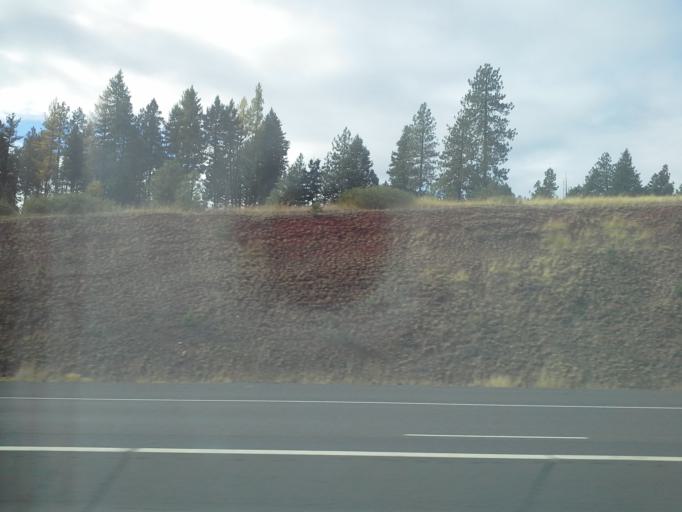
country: US
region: Oregon
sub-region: Union County
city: La Grande
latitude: 45.3941
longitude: -118.3268
